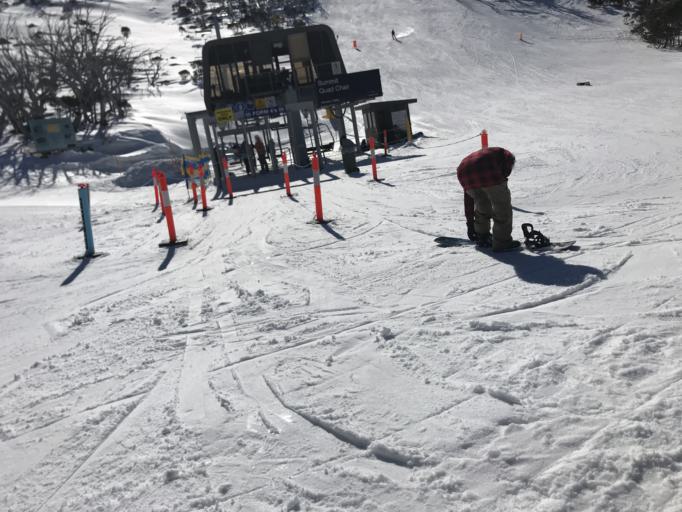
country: AU
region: New South Wales
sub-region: Snowy River
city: Jindabyne
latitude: -36.3826
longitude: 148.3979
